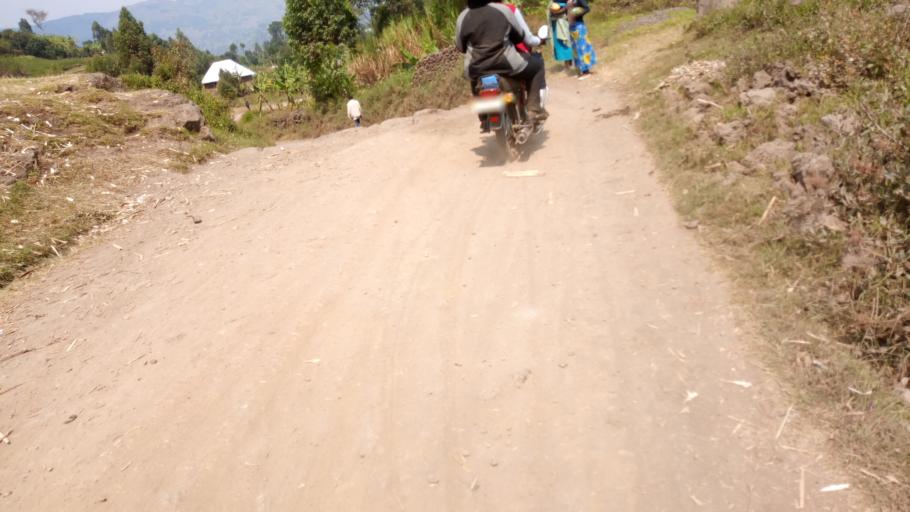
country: UG
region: Western Region
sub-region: Kisoro District
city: Kisoro
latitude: -1.3316
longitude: 29.7604
